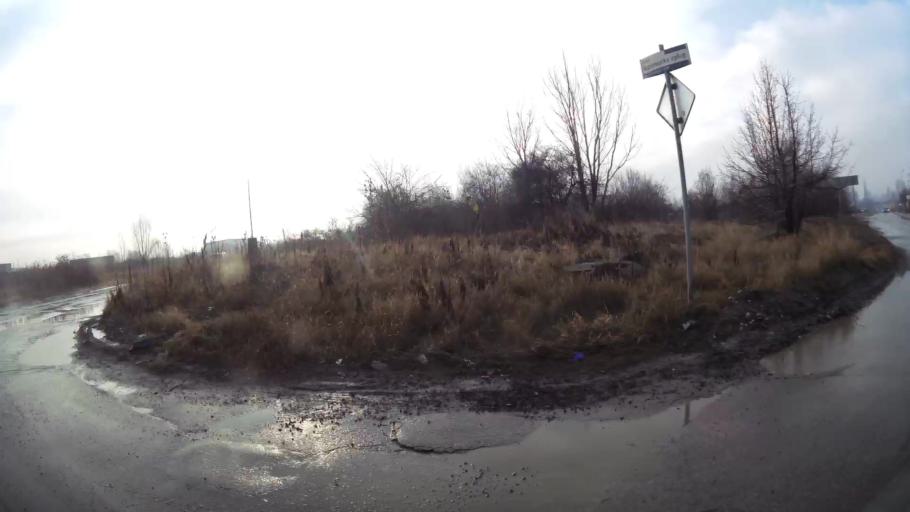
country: BG
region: Sofia-Capital
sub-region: Stolichna Obshtina
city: Sofia
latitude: 42.7418
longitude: 23.3289
